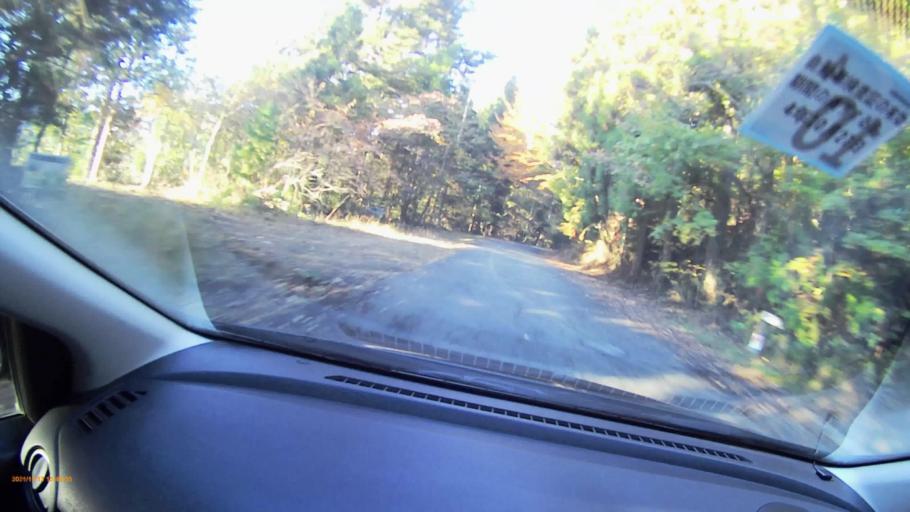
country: JP
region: Gifu
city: Nakatsugawa
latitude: 35.5840
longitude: 137.3887
